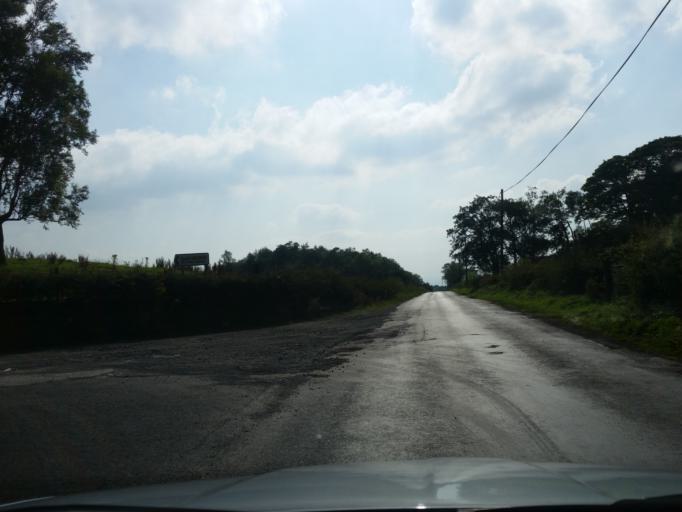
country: GB
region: Northern Ireland
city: Ballinamallard
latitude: 54.3713
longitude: -7.5616
